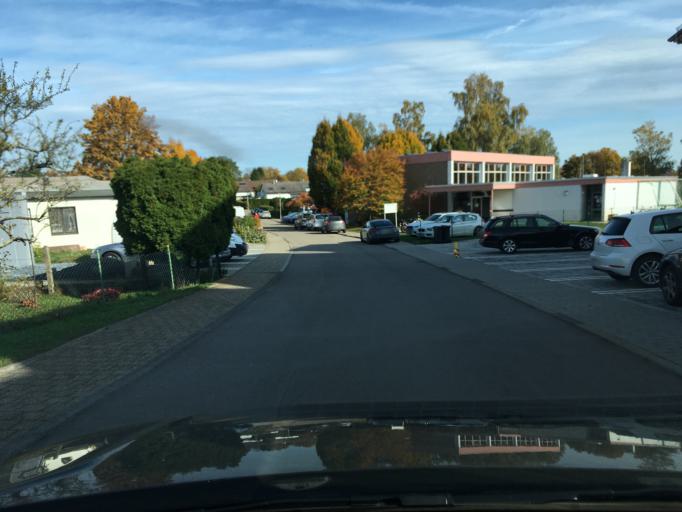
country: DE
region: Baden-Wuerttemberg
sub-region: Regierungsbezirk Stuttgart
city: Siegelsbach
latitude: 49.2432
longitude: 9.0562
